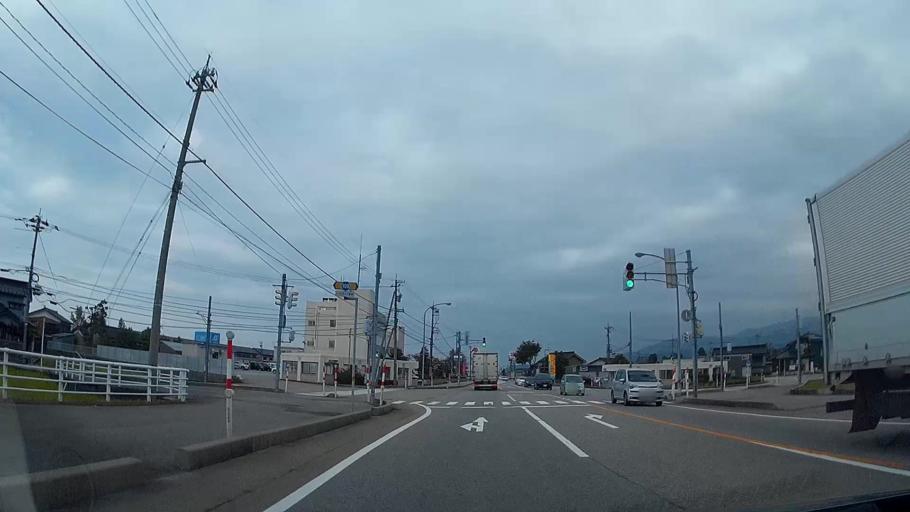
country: JP
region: Toyama
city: Nyuzen
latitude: 36.9386
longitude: 137.5119
